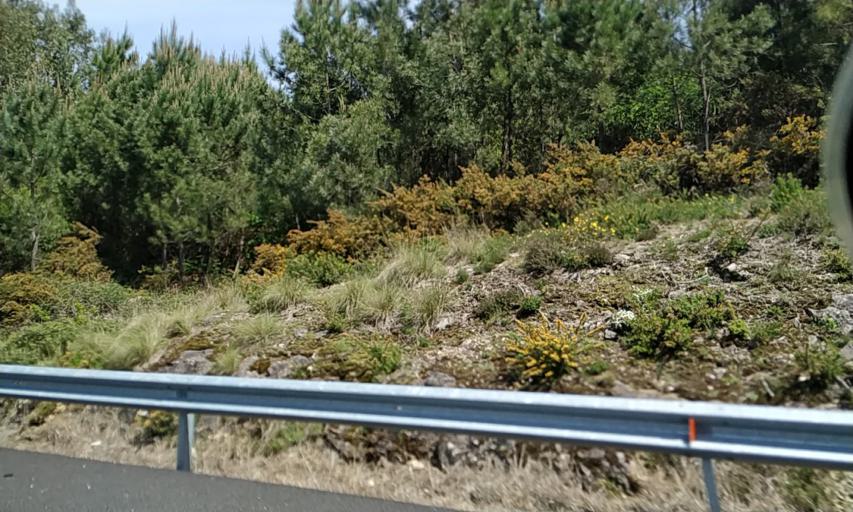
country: ES
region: Galicia
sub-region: Provincia de Pontevedra
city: Valga
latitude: 42.6977
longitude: -8.6361
